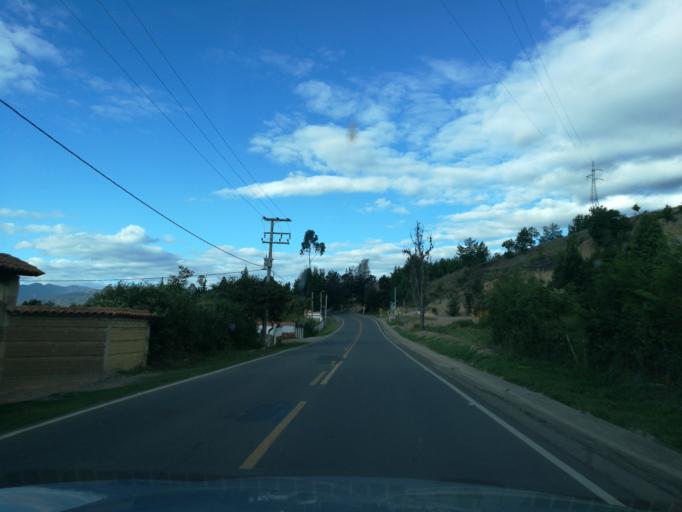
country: CO
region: Boyaca
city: Sutamarchan
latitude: 5.6055
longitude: -73.6347
